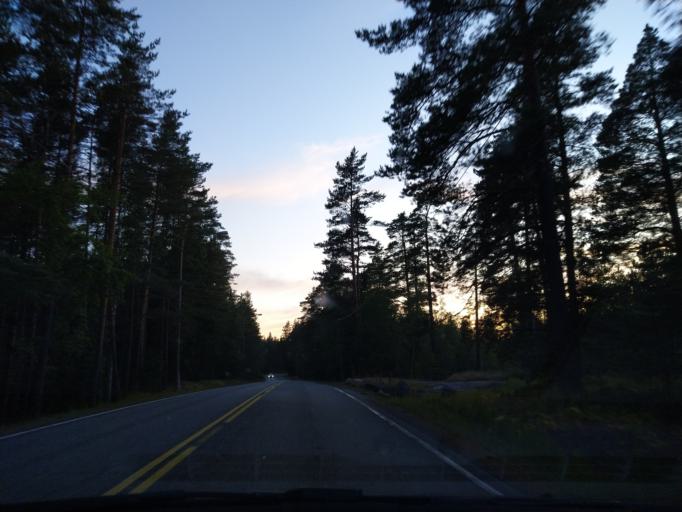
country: FI
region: Uusimaa
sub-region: Helsinki
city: Tuusula
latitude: 60.3529
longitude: 25.0253
